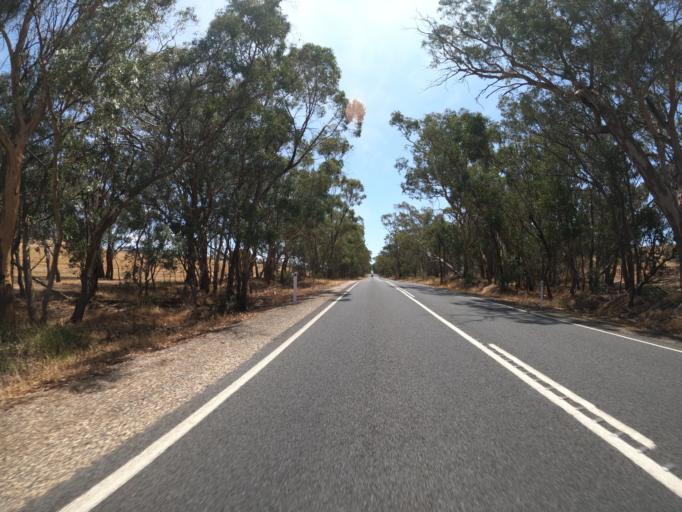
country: AU
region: Victoria
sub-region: Benalla
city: Benalla
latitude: -36.3785
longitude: 145.9760
